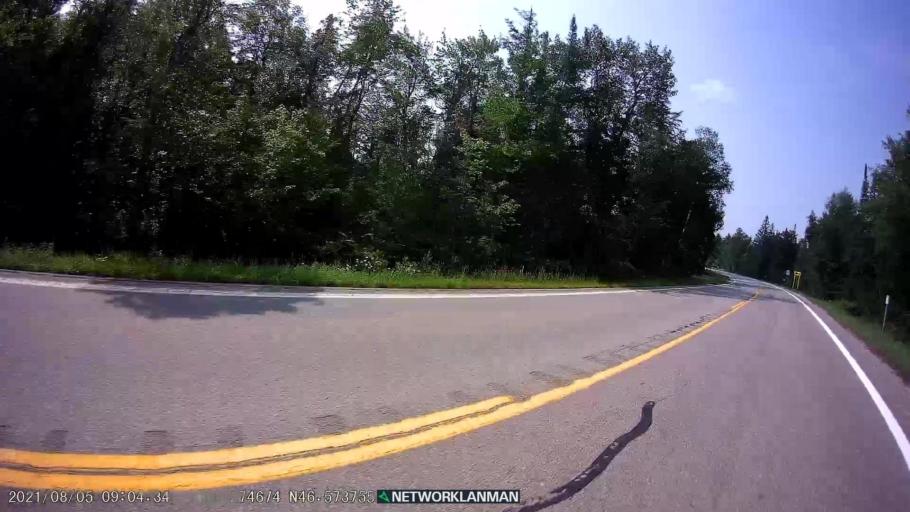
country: US
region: Michigan
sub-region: Luce County
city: Newberry
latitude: 46.5736
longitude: -85.2752
